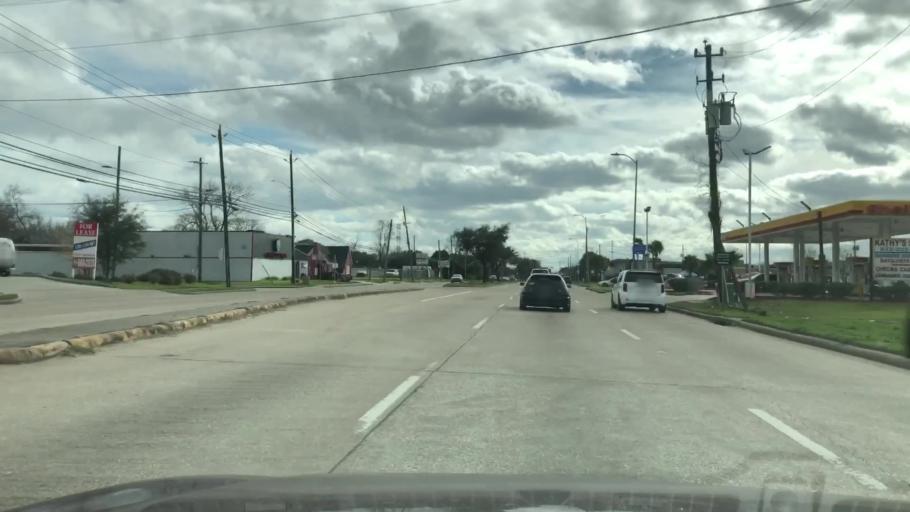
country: US
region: Texas
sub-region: Harris County
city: Bellaire
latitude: 29.6370
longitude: -95.4636
